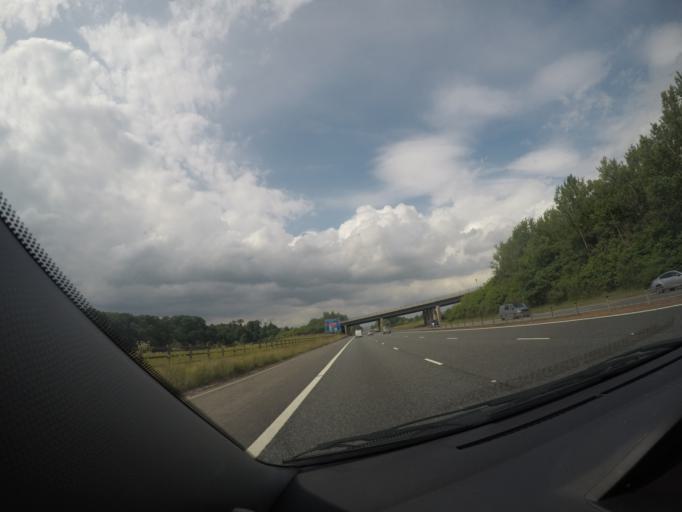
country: GB
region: Scotland
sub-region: Dumfries and Galloway
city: Lochmaben
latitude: 55.2077
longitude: -3.4127
